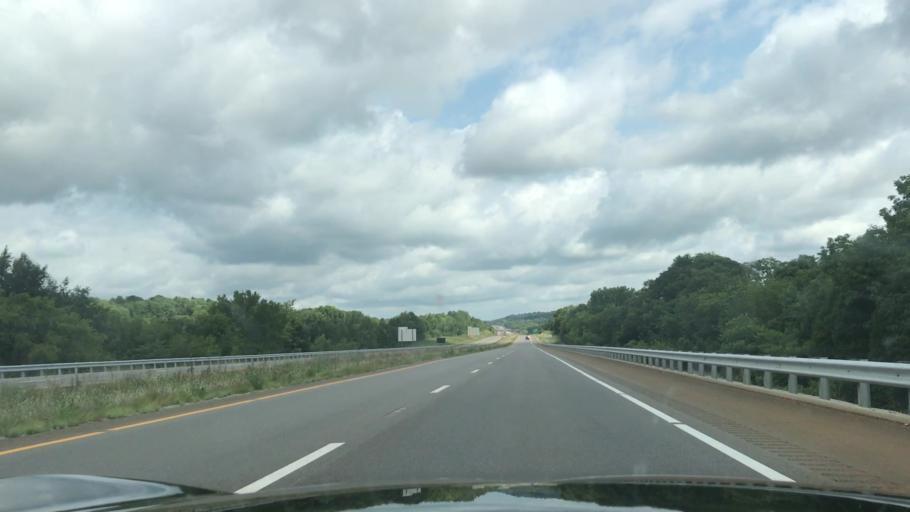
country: US
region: Kentucky
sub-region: Warren County
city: Bowling Green
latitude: 36.9764
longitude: -86.5005
